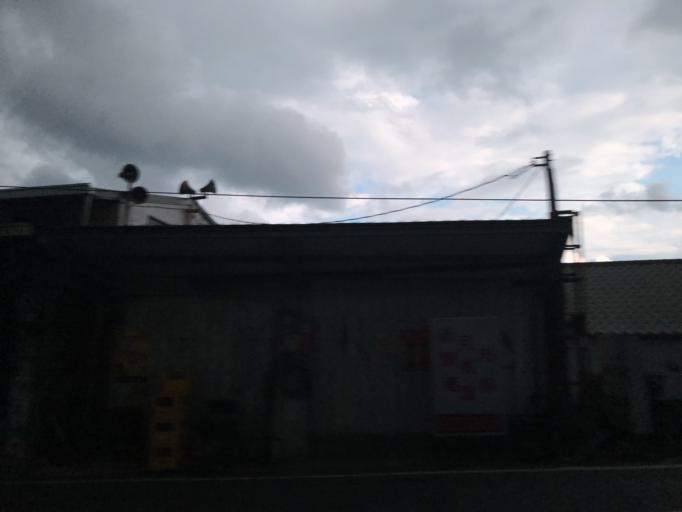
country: TW
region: Taiwan
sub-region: Taitung
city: Taitung
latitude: 22.8607
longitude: 121.2011
